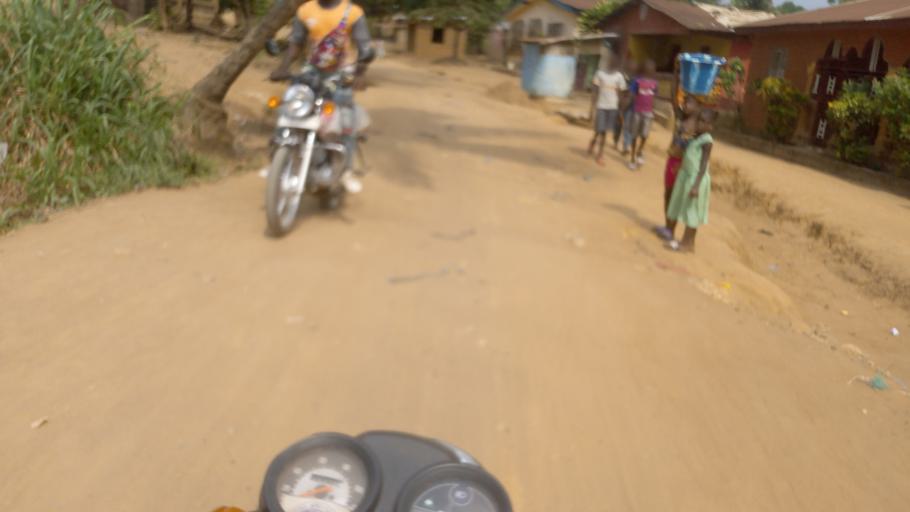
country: SL
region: Western Area
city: Waterloo
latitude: 8.3232
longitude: -13.0578
